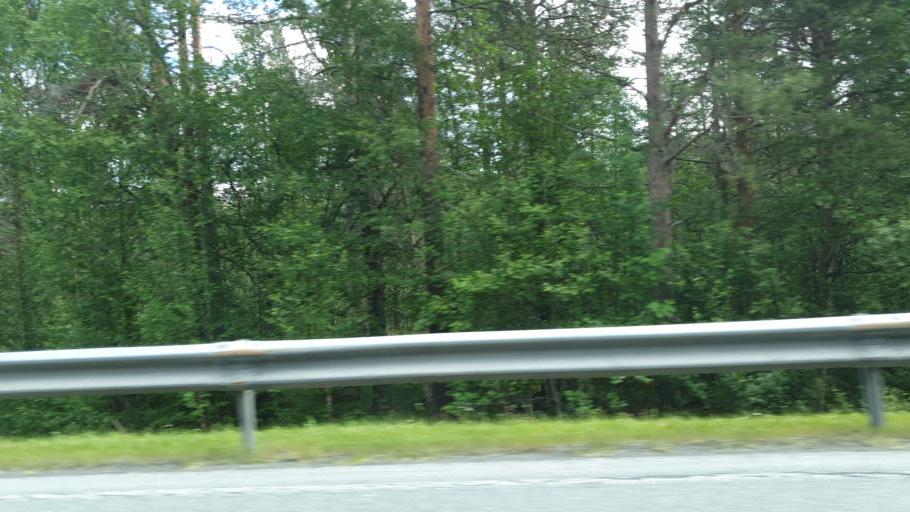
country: NO
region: Sor-Trondelag
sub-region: Rennebu
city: Berkak
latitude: 62.6870
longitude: 9.9309
